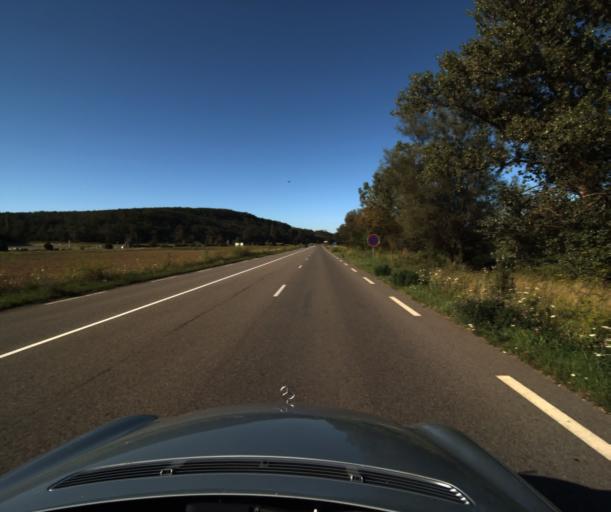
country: FR
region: Midi-Pyrenees
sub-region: Departement de l'Ariege
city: Lavelanet
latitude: 43.0042
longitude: 1.8831
